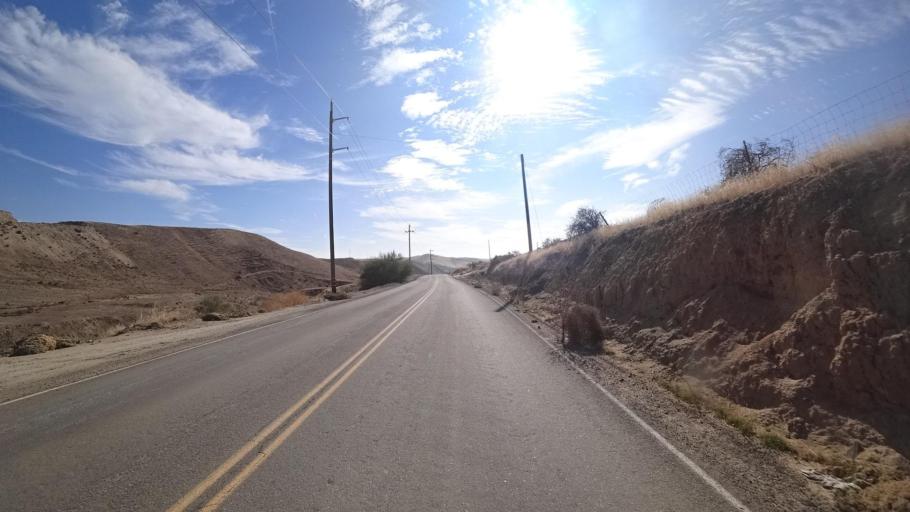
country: US
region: California
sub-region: Kern County
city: Oildale
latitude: 35.5460
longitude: -118.9588
